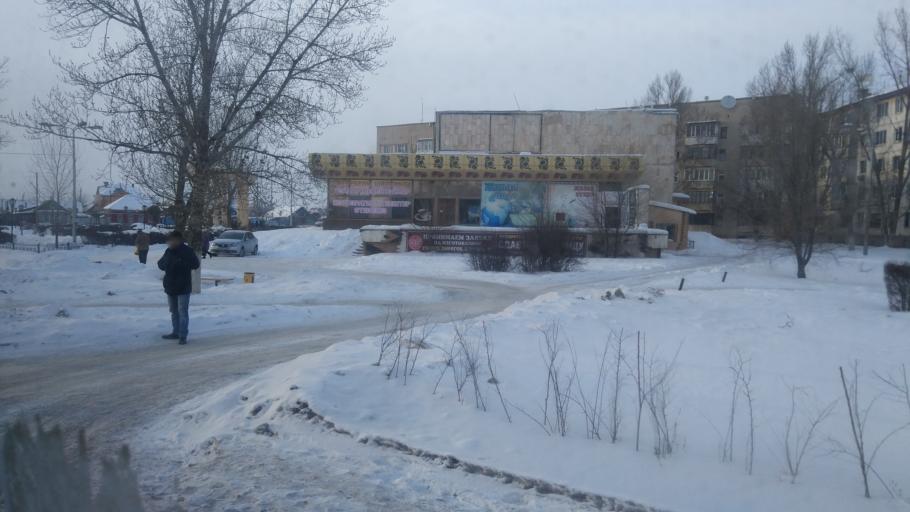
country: KZ
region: Batys Qazaqstan
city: Oral
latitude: 51.2384
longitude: 51.3985
